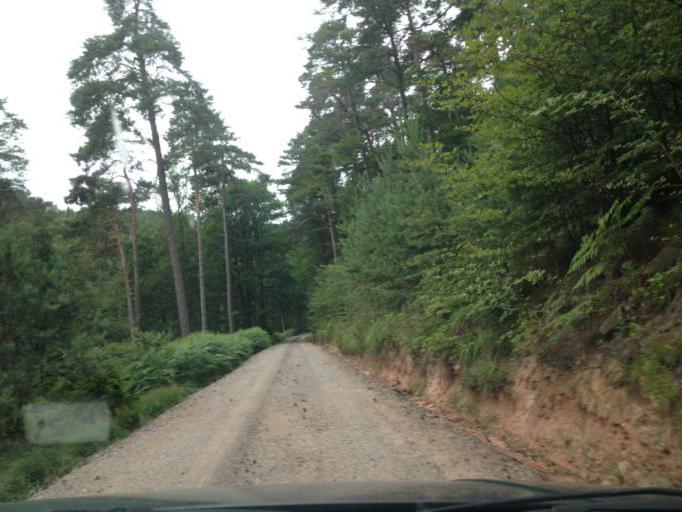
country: DE
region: Rheinland-Pfalz
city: Elmstein
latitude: 49.3054
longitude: 7.8725
